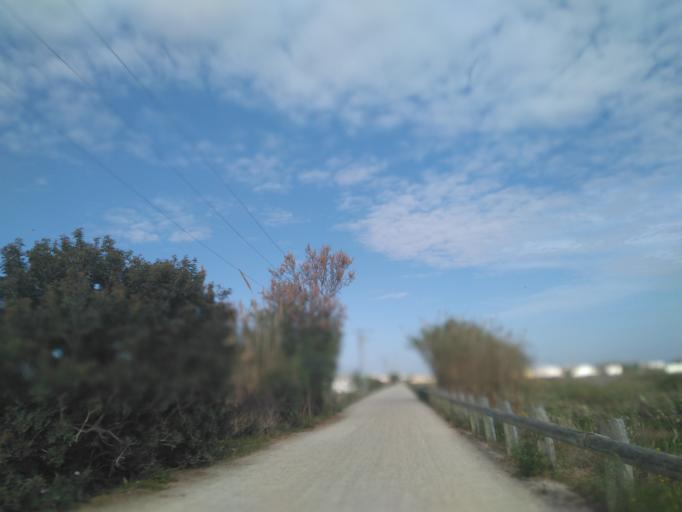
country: ES
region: Valencia
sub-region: Provincia de Valencia
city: Alboraya
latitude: 39.5029
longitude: -0.3357
